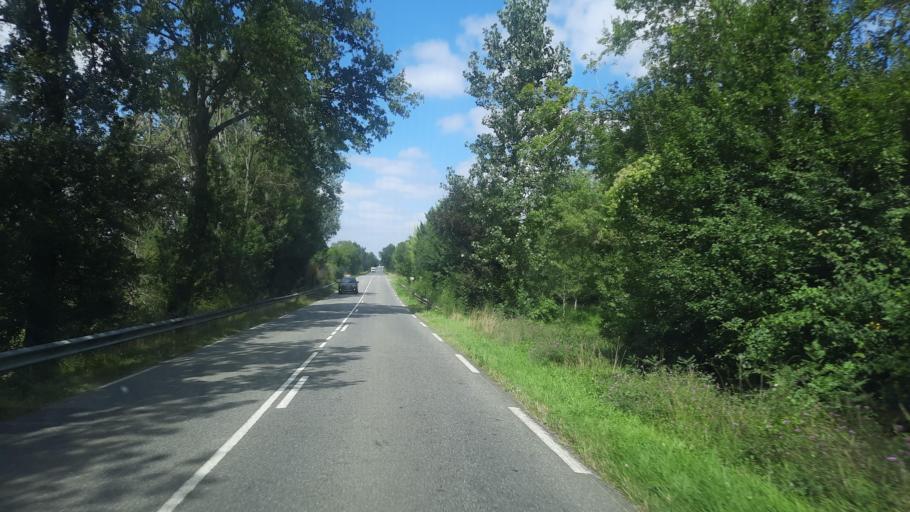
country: FR
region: Midi-Pyrenees
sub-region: Departement du Gers
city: Samatan
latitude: 43.5042
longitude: 0.9729
